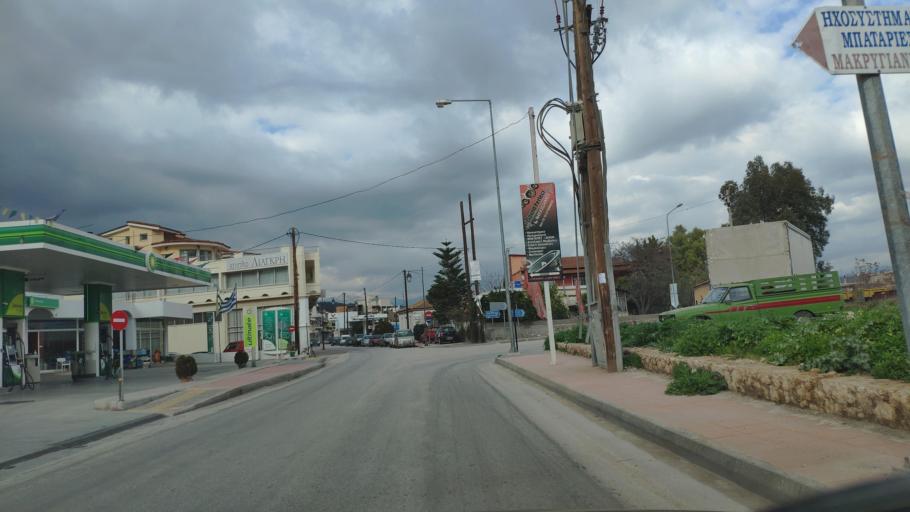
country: GR
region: Peloponnese
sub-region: Nomos Argolidos
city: Argos
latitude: 37.6294
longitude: 22.7367
